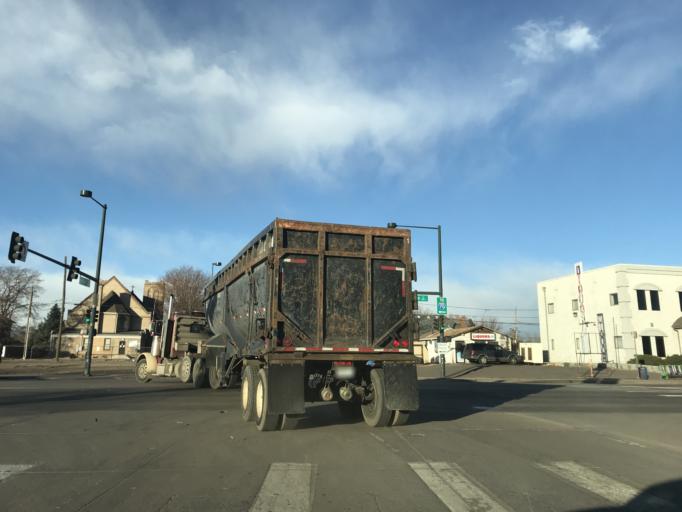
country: US
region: Colorado
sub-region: Denver County
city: Denver
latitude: 39.7818
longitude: -104.9784
